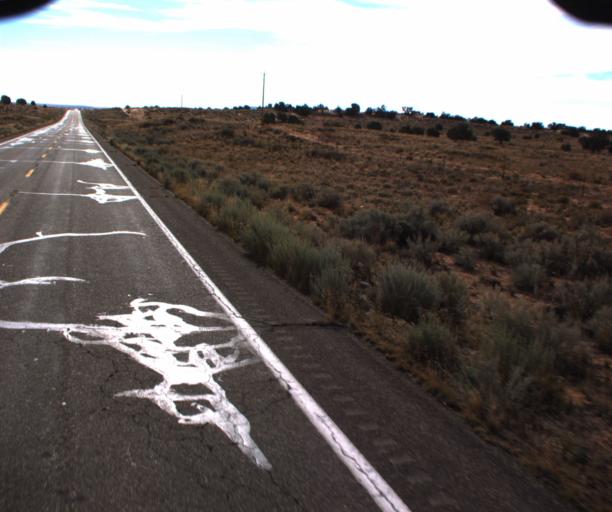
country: US
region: Arizona
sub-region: Coconino County
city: Kaibito
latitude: 36.6186
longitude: -111.1957
